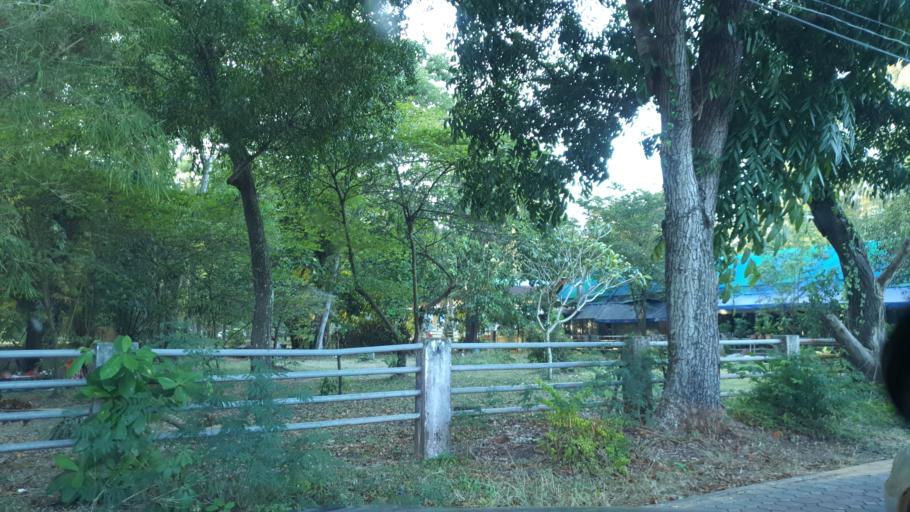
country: TH
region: Krabi
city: Krabi
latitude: 8.0533
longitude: 98.9197
